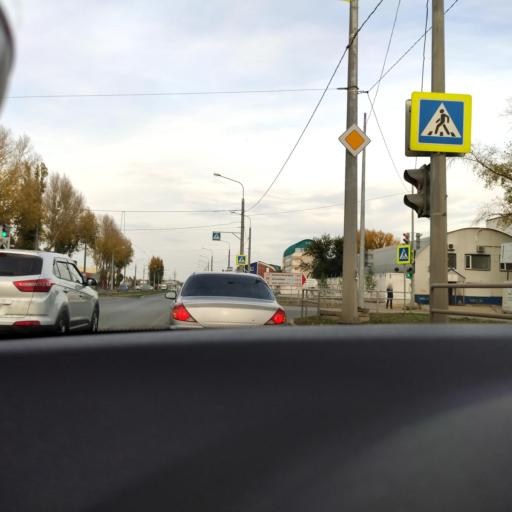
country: RU
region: Samara
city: Samara
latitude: 53.1989
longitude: 50.2558
